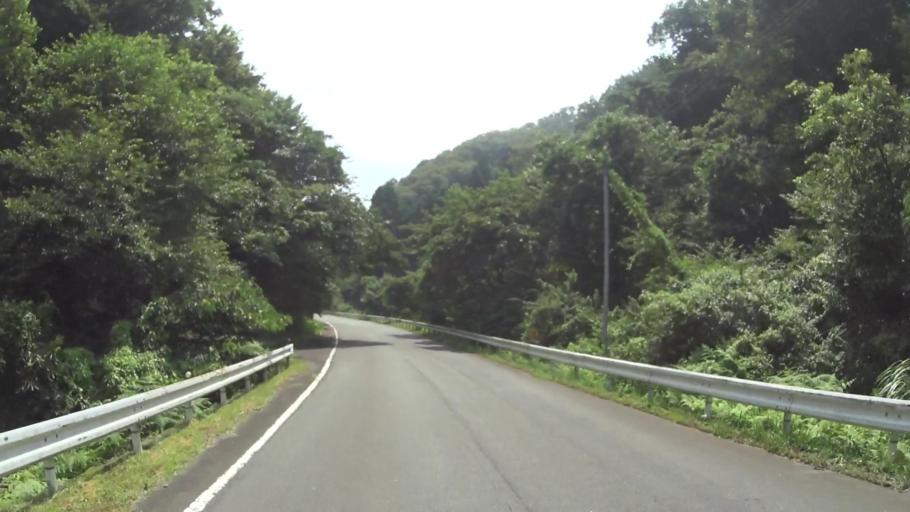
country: JP
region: Kyoto
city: Ayabe
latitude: 35.2015
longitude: 135.3754
